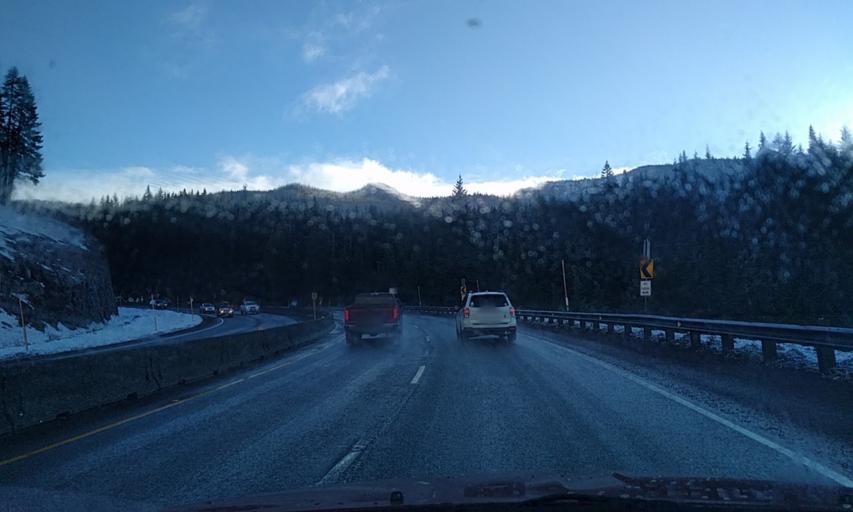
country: US
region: Oregon
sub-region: Clackamas County
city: Mount Hood Village
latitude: 45.3084
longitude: -121.7927
